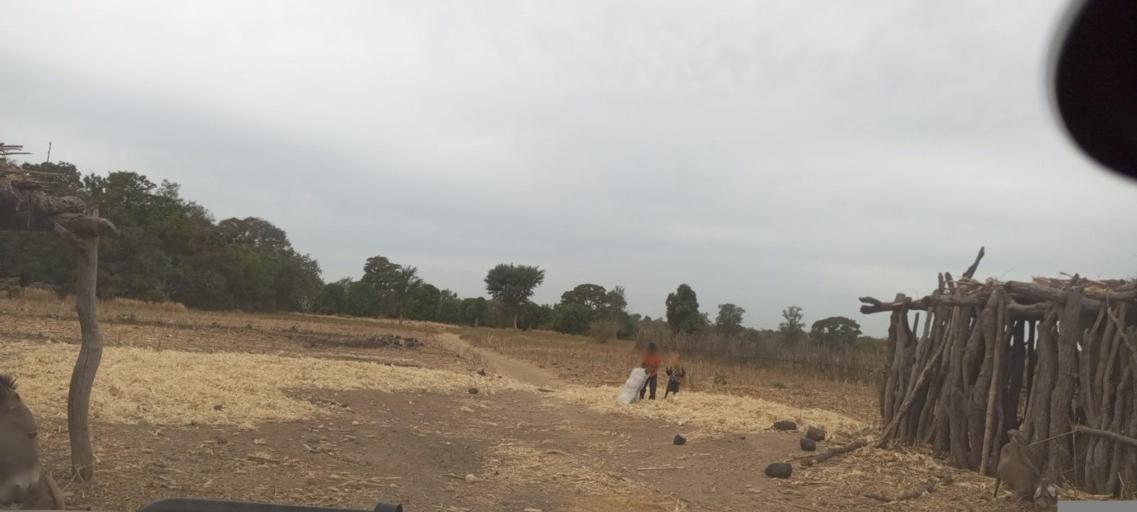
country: ML
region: Koulikoro
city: Kati
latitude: 12.7699
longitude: -8.3697
